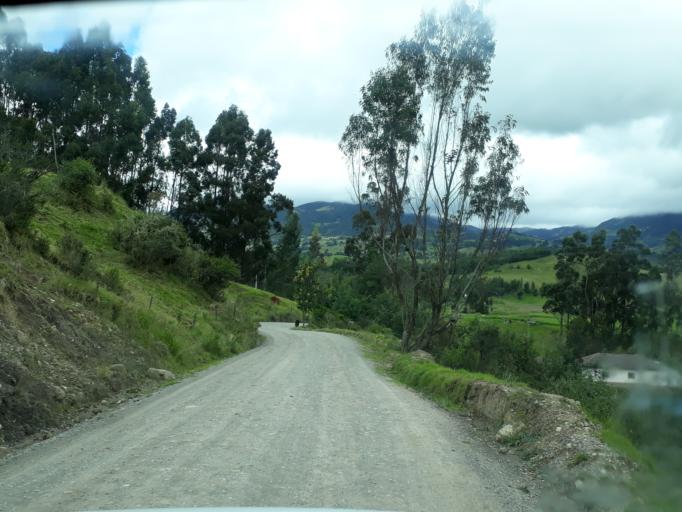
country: CO
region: Cundinamarca
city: Carmen de Carupa
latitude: 5.3084
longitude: -73.8979
